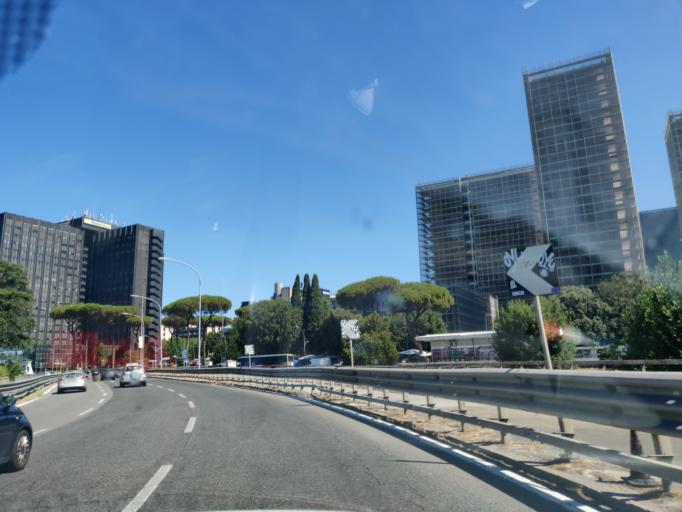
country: IT
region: Latium
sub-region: Citta metropolitana di Roma Capitale
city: Selcetta
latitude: 41.8284
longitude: 12.4696
